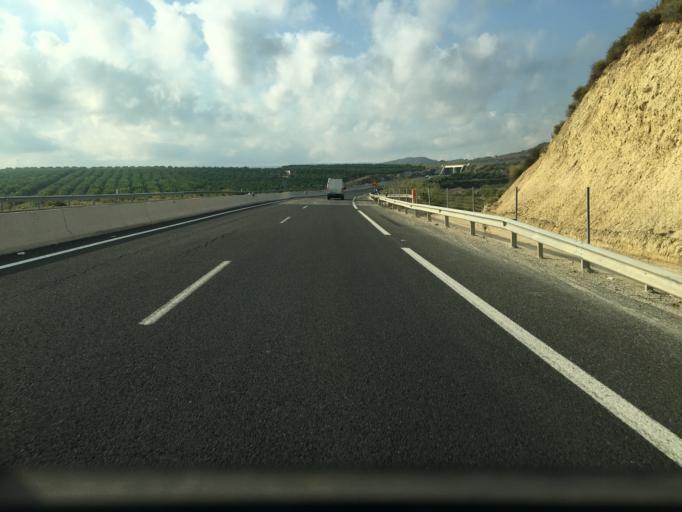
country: ES
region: Murcia
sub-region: Murcia
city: Beniel
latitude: 37.9925
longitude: -0.9759
